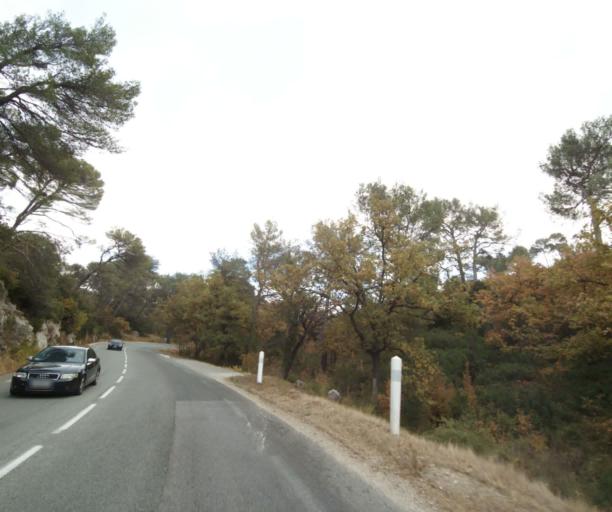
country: FR
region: Provence-Alpes-Cote d'Azur
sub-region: Departement des Bouches-du-Rhone
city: Cuges-les-Pins
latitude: 43.2656
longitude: 5.6622
